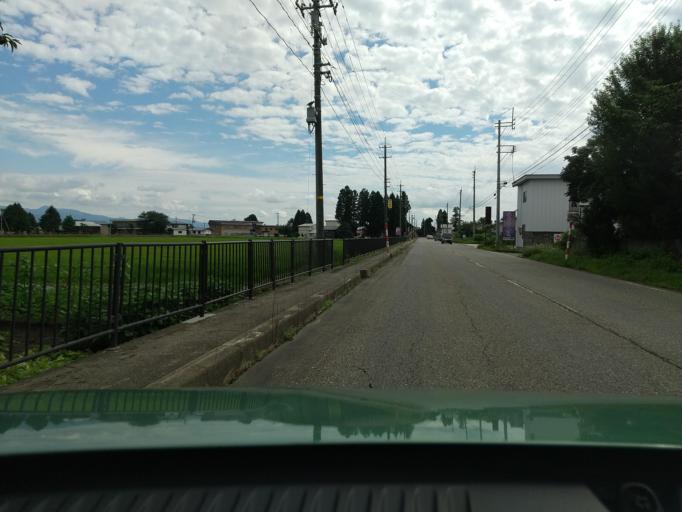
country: JP
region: Akita
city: Kakunodatemachi
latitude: 39.5638
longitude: 140.5590
